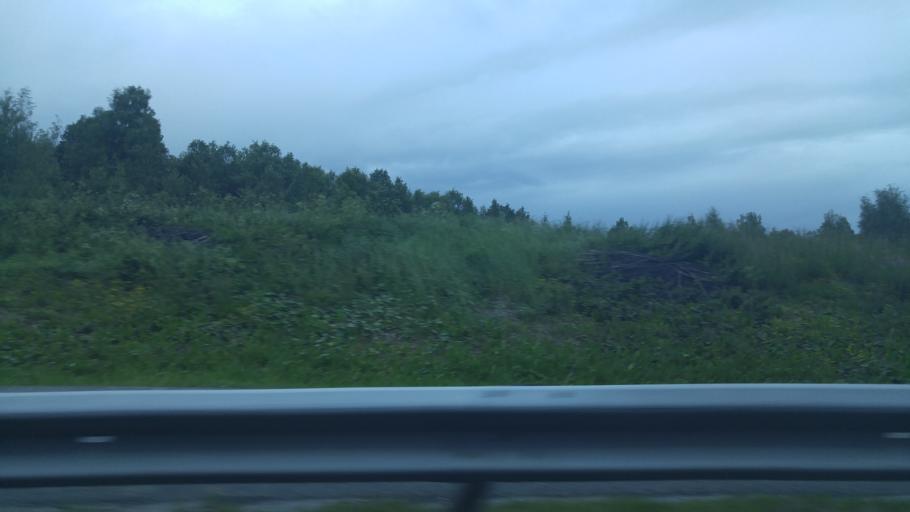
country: NO
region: Sor-Trondelag
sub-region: Malvik
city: Hommelvik
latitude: 63.4113
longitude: 10.8169
